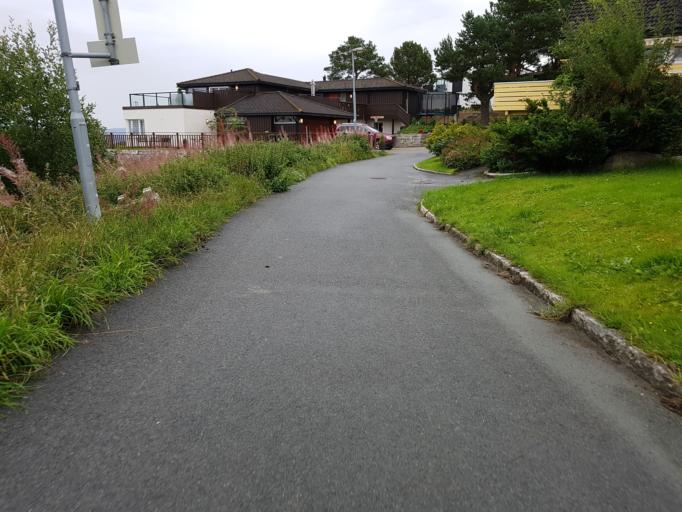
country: NO
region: Sor-Trondelag
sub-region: Trondheim
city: Trondheim
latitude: 63.4098
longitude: 10.4863
